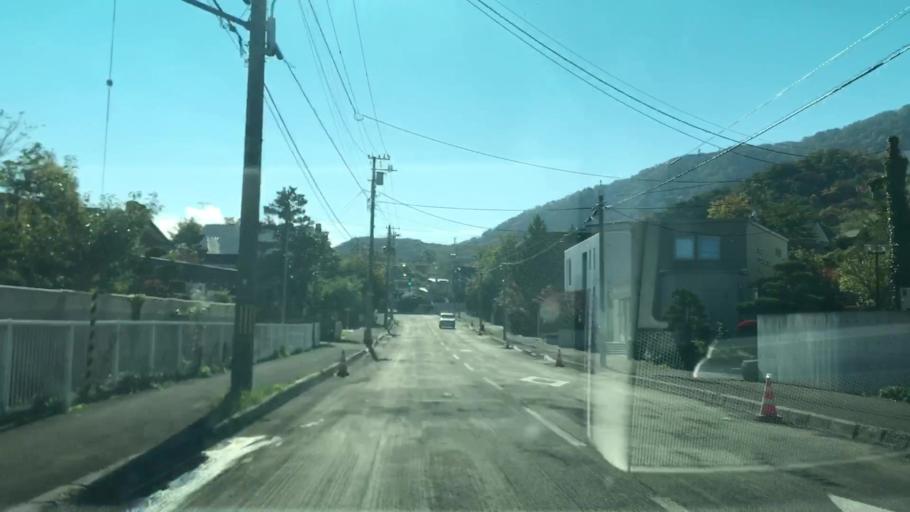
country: JP
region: Hokkaido
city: Sapporo
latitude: 43.0398
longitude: 141.3209
